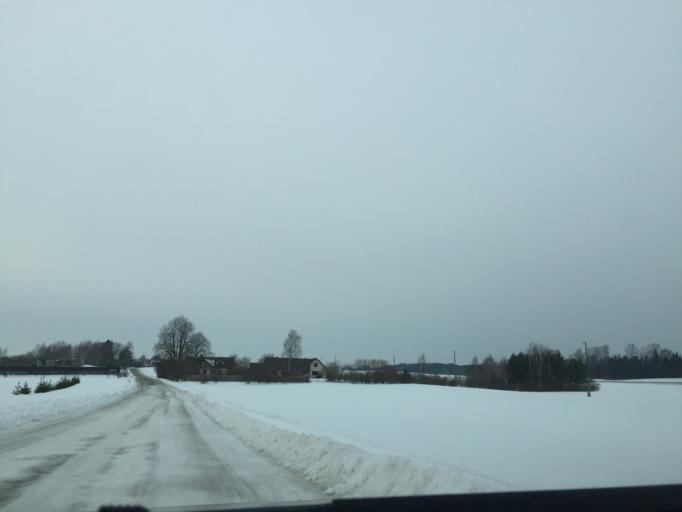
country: LV
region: Ikskile
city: Ikskile
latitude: 56.8451
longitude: 24.4557
